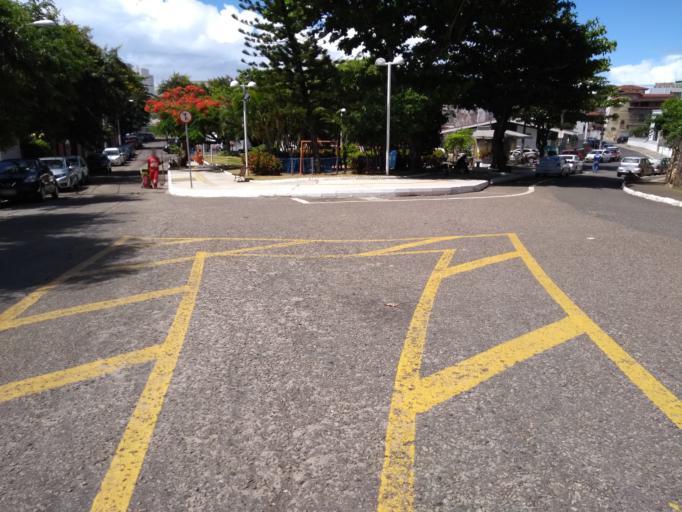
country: BR
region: Bahia
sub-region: Salvador
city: Salvador
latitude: -13.0098
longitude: -38.4897
